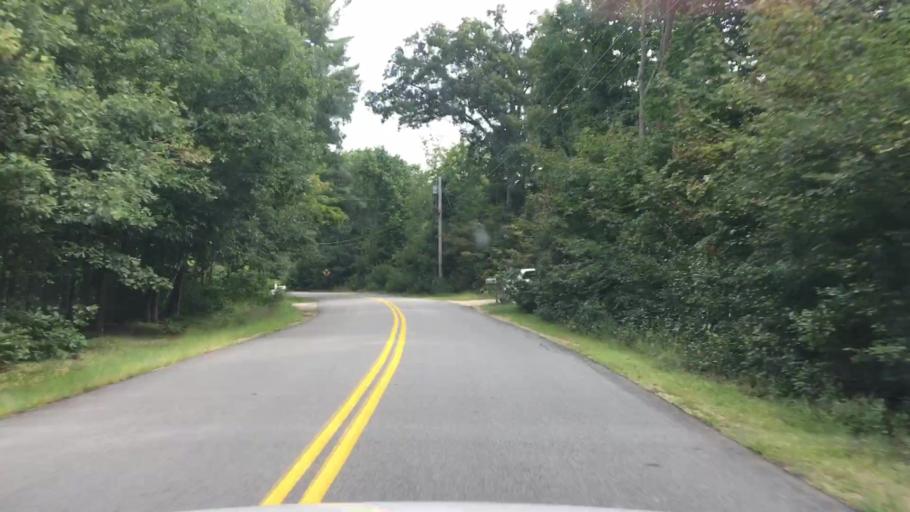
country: US
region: New Hampshire
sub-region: Strafford County
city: Barrington
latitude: 43.1988
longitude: -70.9928
